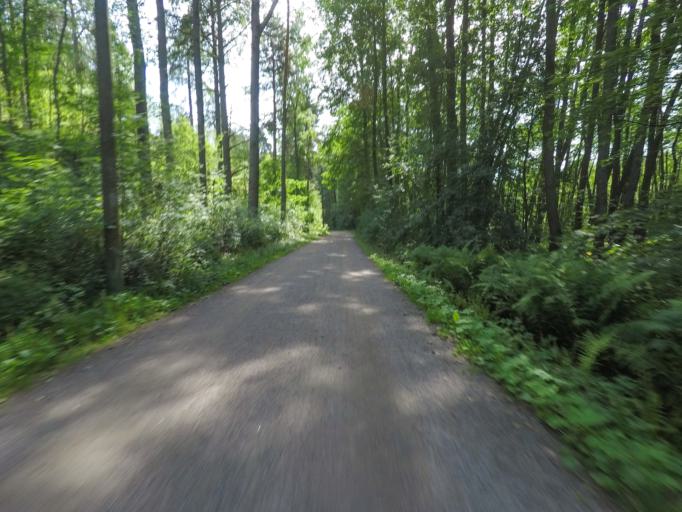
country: FI
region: Uusimaa
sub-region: Helsinki
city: Vantaa
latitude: 60.2082
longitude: 25.0282
